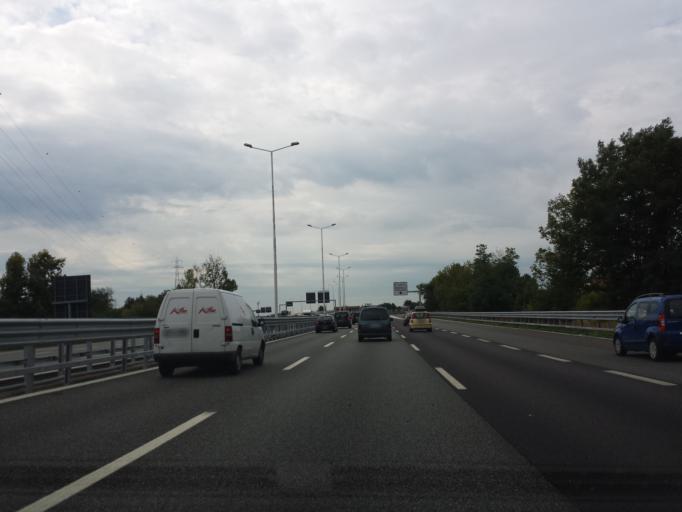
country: IT
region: Lombardy
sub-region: Citta metropolitana di Milano
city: Figino
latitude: 45.4923
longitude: 9.0665
